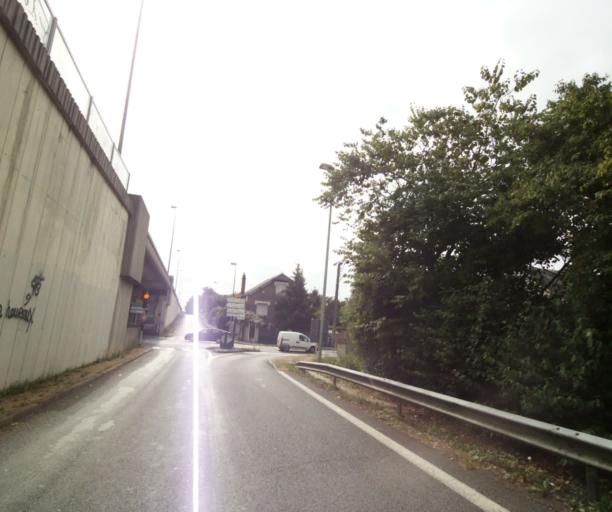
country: FR
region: Centre
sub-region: Departement du Loiret
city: Fleury-les-Aubrais
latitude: 47.9375
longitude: 1.9179
